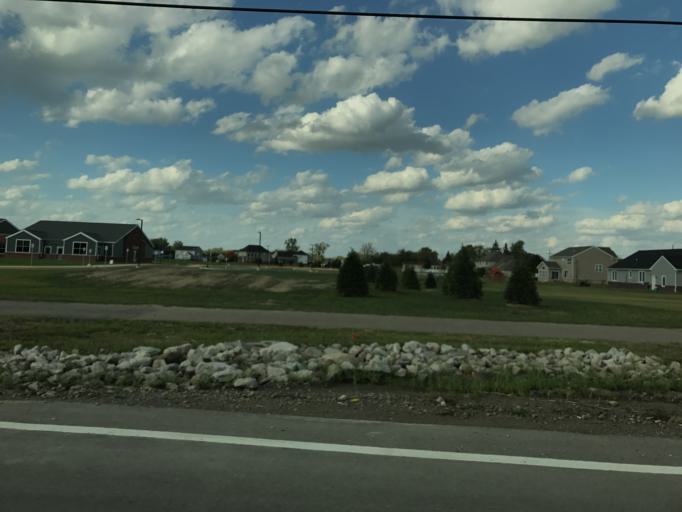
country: US
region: Michigan
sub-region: Oakland County
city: South Lyon
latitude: 42.4763
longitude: -83.6192
